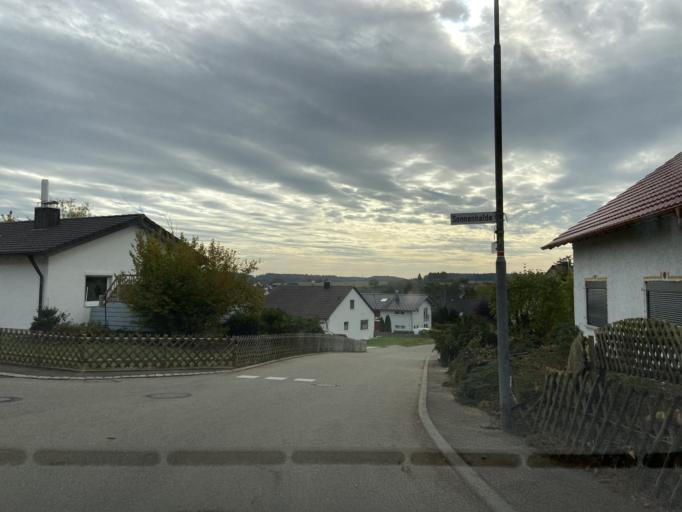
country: DE
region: Baden-Wuerttemberg
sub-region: Tuebingen Region
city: Bingen
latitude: 48.1122
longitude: 9.2645
